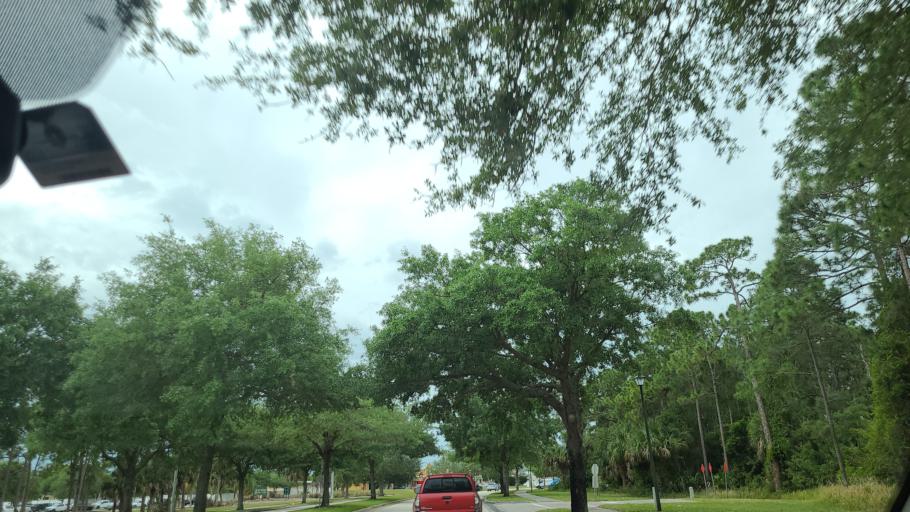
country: US
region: Florida
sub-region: Brevard County
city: Grant-Valkaria
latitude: 27.9528
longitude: -80.6545
